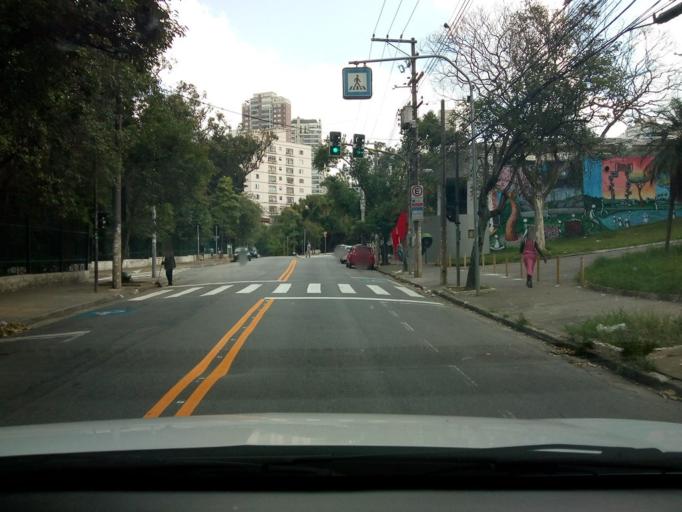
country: BR
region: Sao Paulo
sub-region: Sao Paulo
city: Sao Paulo
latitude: -23.5728
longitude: -46.6297
